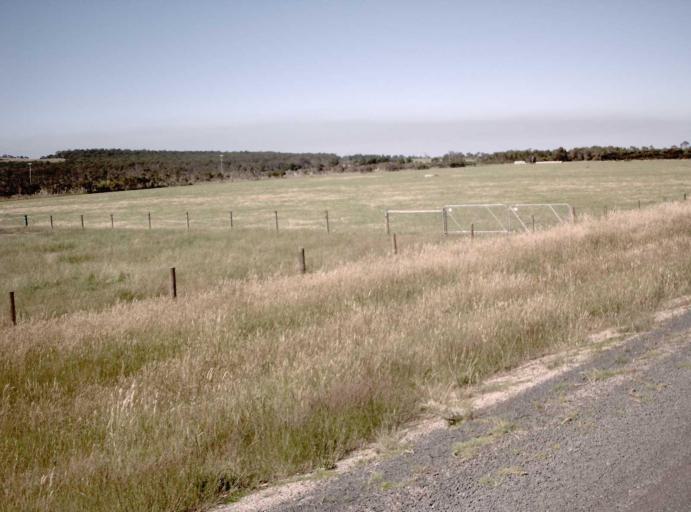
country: AU
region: Victoria
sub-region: Latrobe
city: Morwell
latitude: -38.6320
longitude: 146.5594
